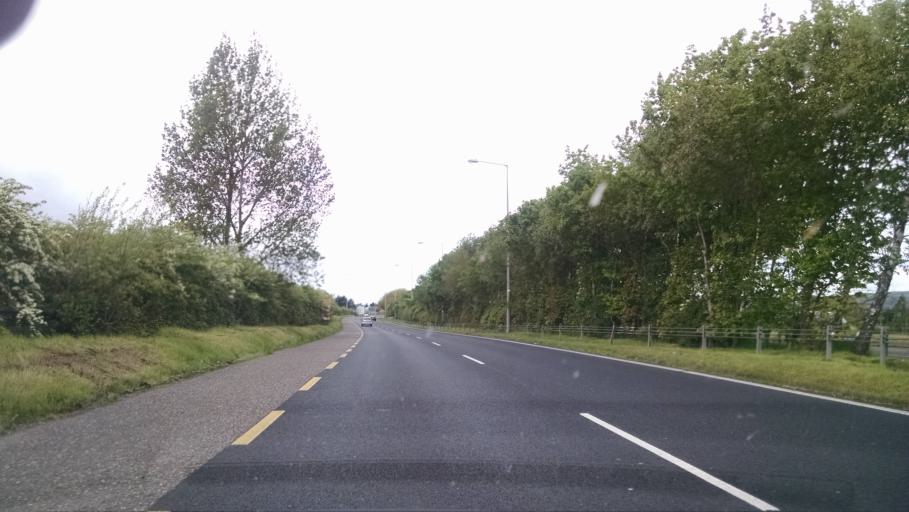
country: IE
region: Munster
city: Moyross
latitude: 52.6781
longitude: -8.6895
